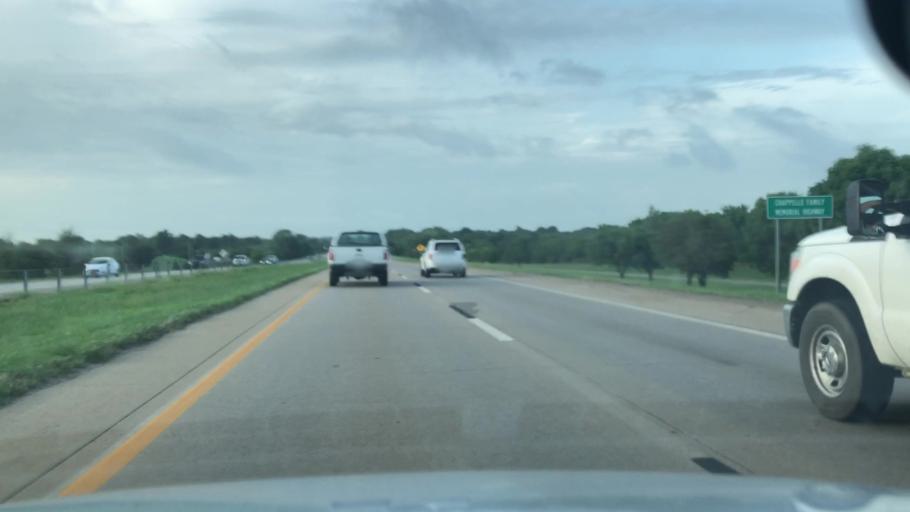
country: US
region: Oklahoma
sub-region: Tulsa County
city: Turley
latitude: 36.2348
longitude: -95.9455
